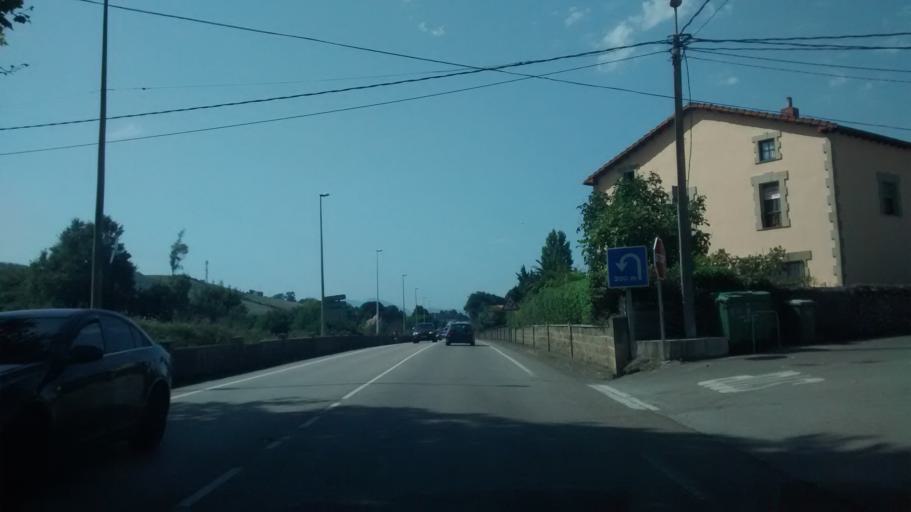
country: ES
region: Cantabria
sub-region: Provincia de Cantabria
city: Arnuero
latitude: 43.4571
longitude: -3.5529
